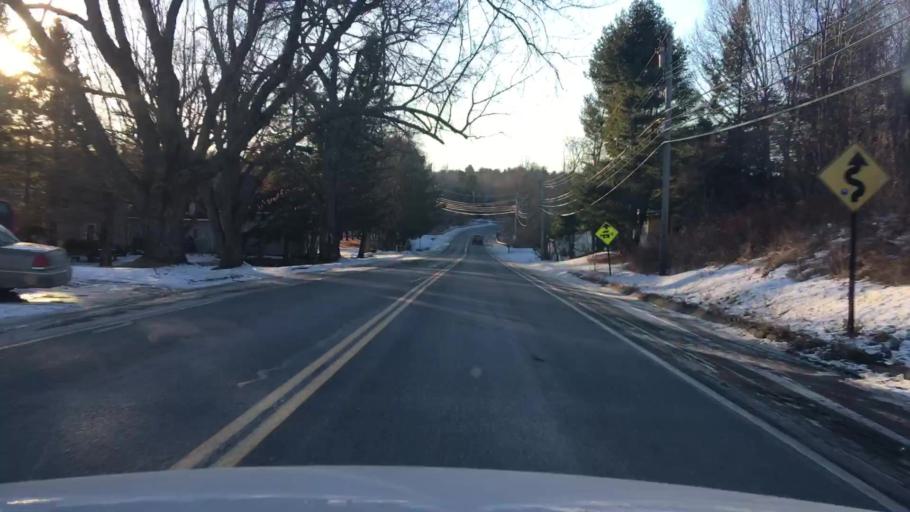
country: US
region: Maine
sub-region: Penobscot County
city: Eddington
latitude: 44.8183
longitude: -68.7047
